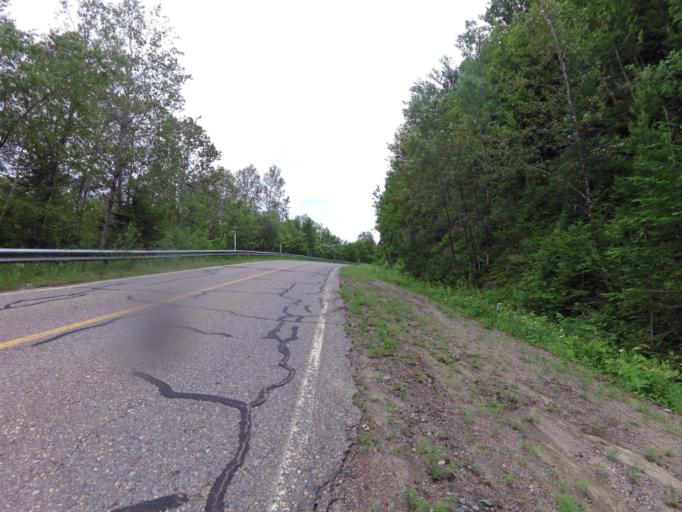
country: CA
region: Quebec
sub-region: Laurentides
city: Brownsburg-Chatham
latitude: 45.8912
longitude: -74.5926
